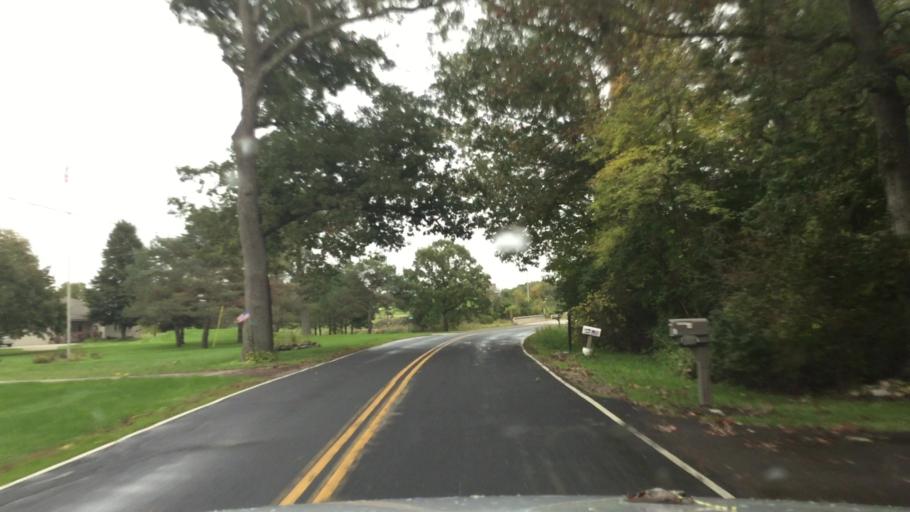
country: US
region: Wisconsin
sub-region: Racine County
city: Waterford
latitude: 42.7639
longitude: -88.1686
